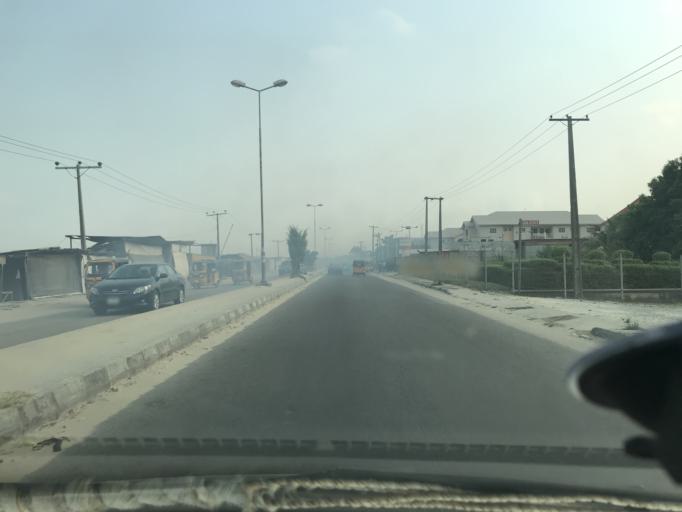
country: NG
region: Lagos
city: Ikoyi
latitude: 6.4791
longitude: 3.5705
